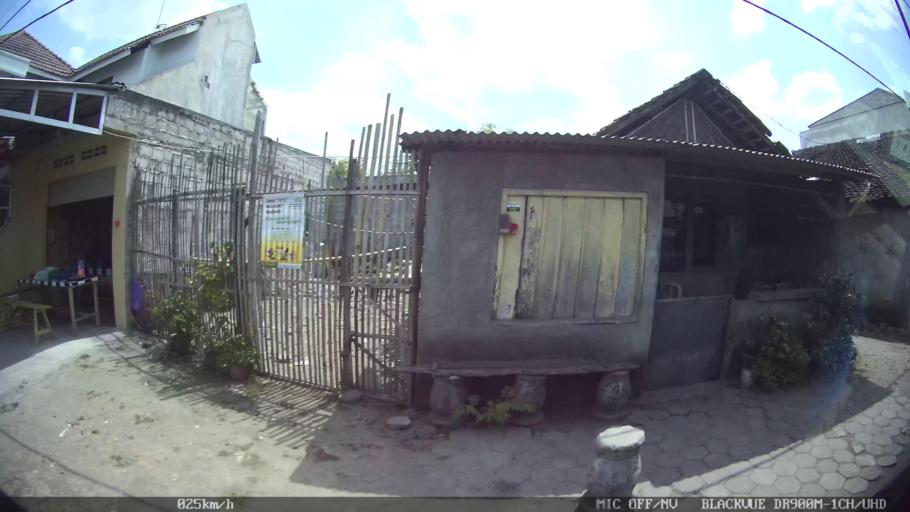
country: ID
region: Daerah Istimewa Yogyakarta
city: Kasihan
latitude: -7.8241
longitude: 110.3460
